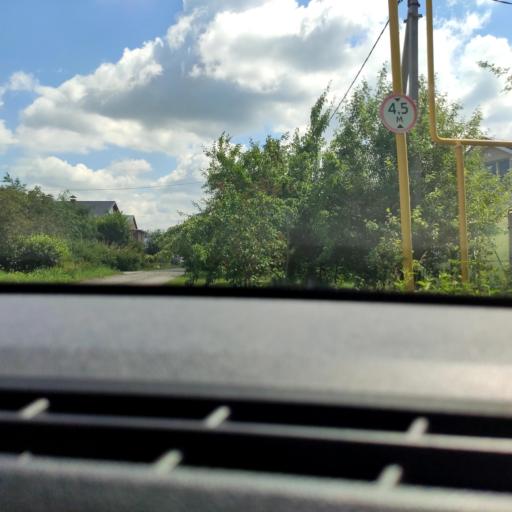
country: RU
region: Samara
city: Podstepki
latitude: 53.5693
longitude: 49.0792
